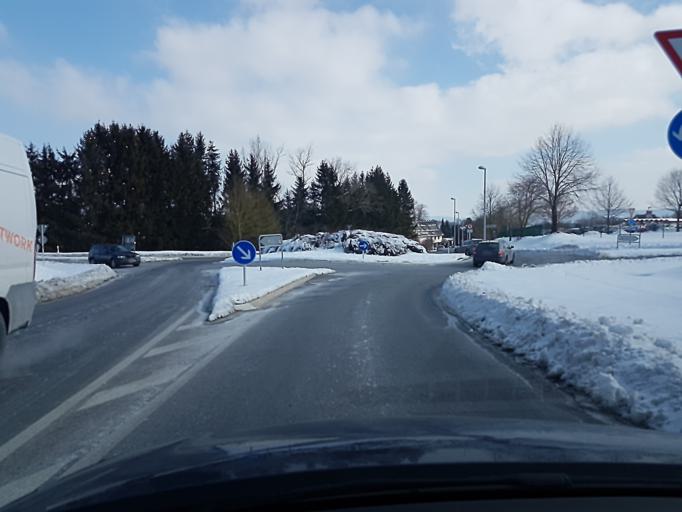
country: DE
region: Baden-Wuerttemberg
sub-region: Freiburg Region
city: Oberndorf
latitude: 48.2920
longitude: 8.5501
